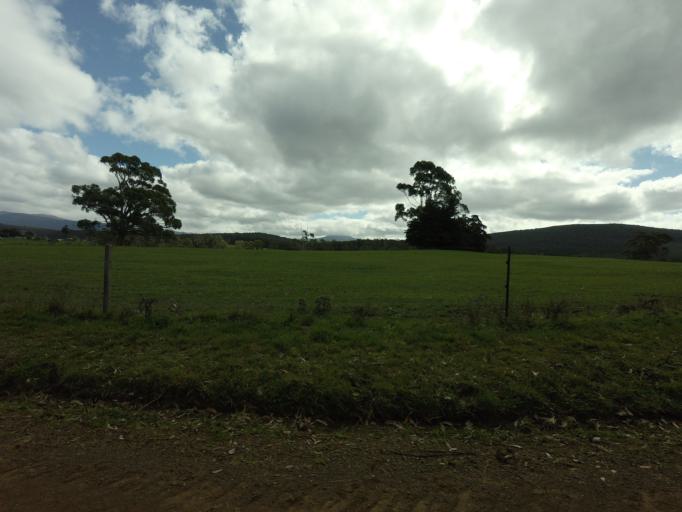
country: AU
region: Tasmania
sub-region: Huon Valley
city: Geeveston
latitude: -43.4324
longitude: 146.9891
